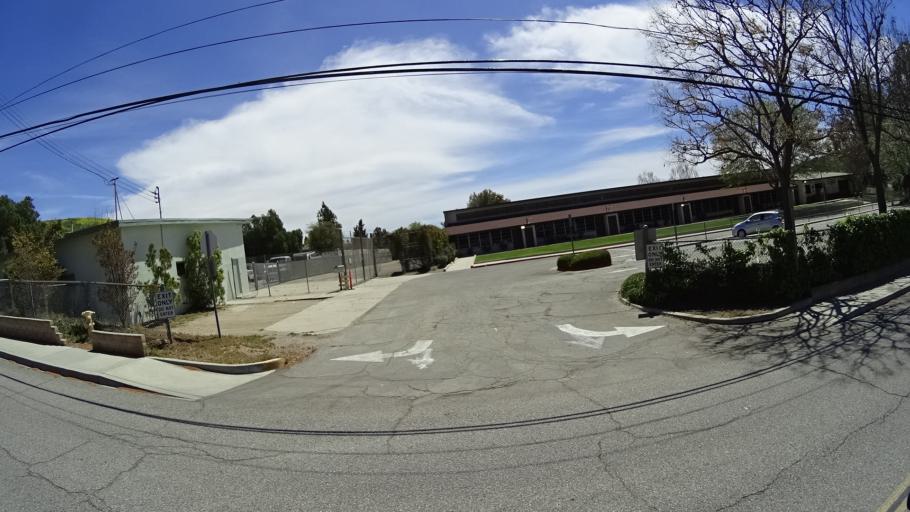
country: US
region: California
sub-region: Ventura County
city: Thousand Oaks
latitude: 34.1787
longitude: -118.8422
